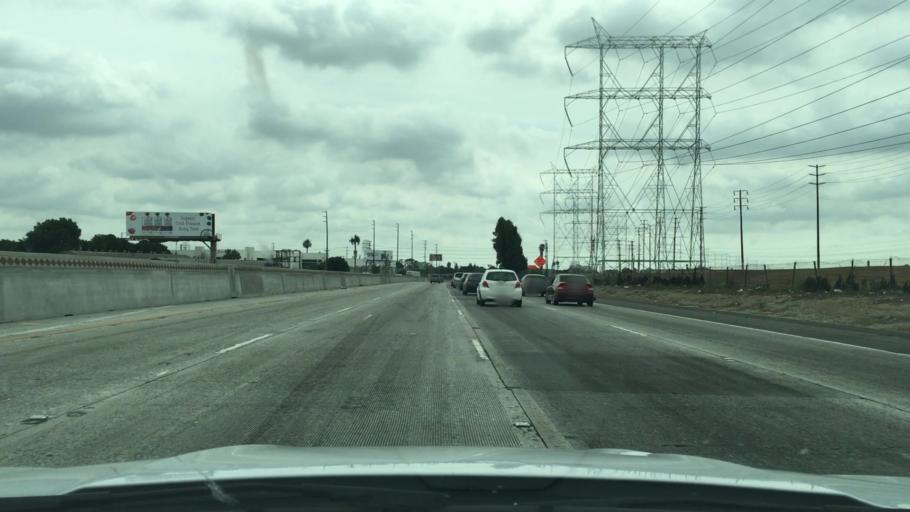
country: US
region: California
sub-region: Los Angeles County
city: Maywood
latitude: 33.9840
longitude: -118.1686
